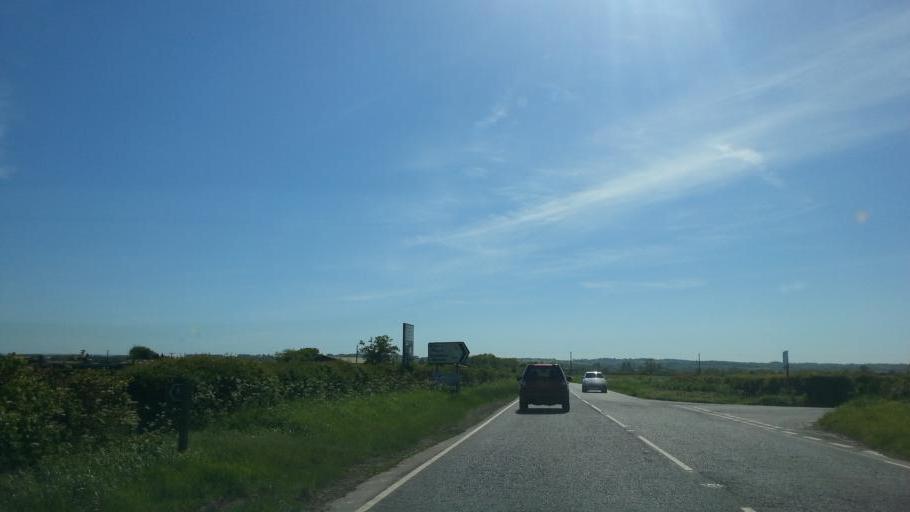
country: GB
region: England
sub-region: Dorset
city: Stalbridge
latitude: 50.9963
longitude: -2.3377
